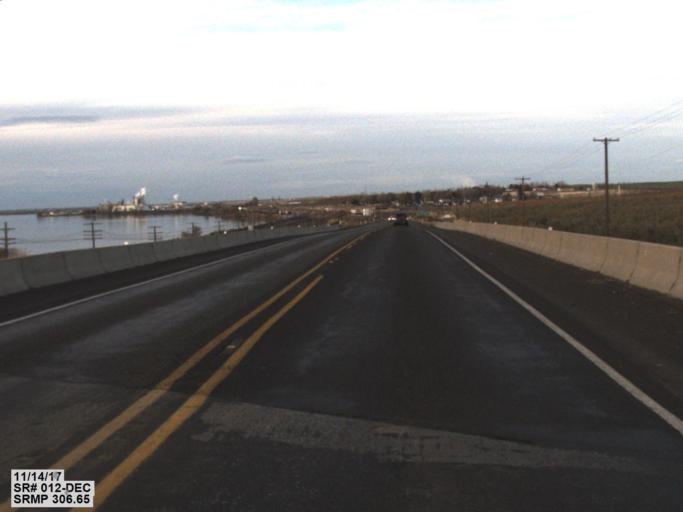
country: US
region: Washington
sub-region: Benton County
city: Finley
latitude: 46.0698
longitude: -118.9079
